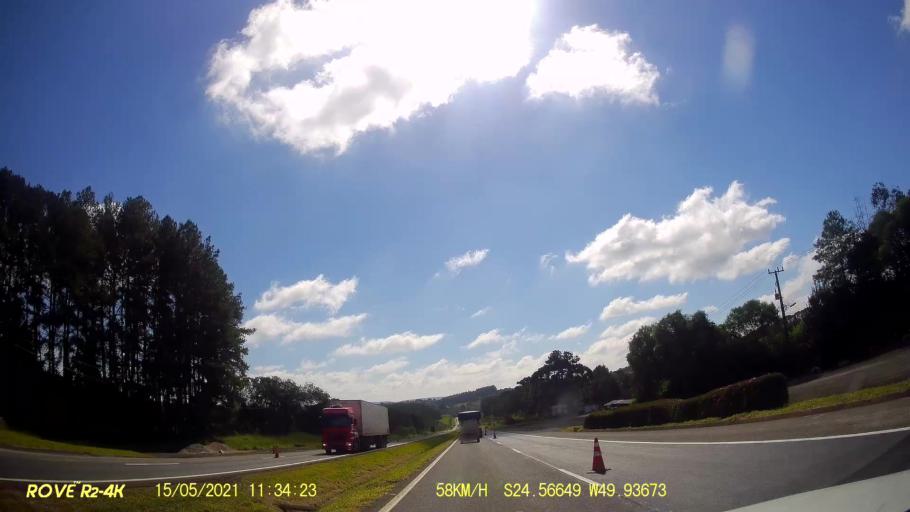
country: BR
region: Parana
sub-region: Pirai Do Sul
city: Pirai do Sul
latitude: -24.5665
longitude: -49.9368
